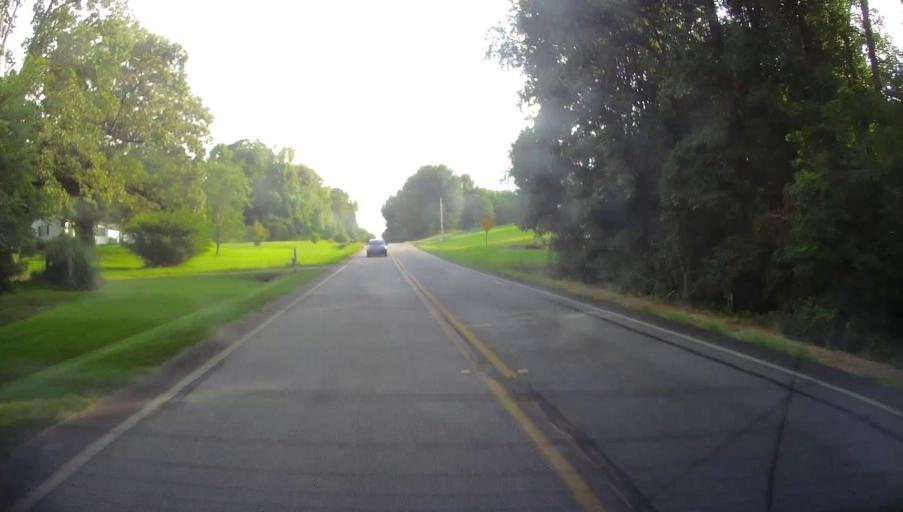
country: US
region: Georgia
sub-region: Crawford County
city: Knoxville
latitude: 32.8596
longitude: -83.9983
